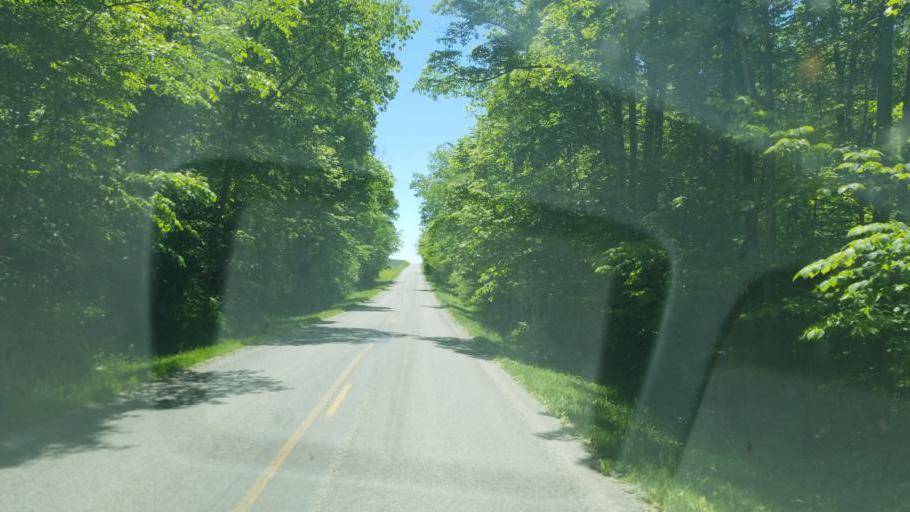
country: US
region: Ohio
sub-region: Mercer County
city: Fort Recovery
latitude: 40.3222
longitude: -84.8035
